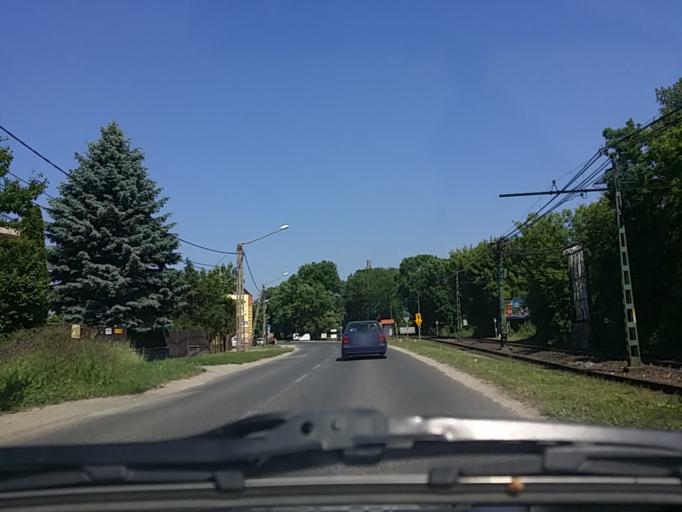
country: HU
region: Pest
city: Pomaz
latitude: 47.6387
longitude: 19.0381
